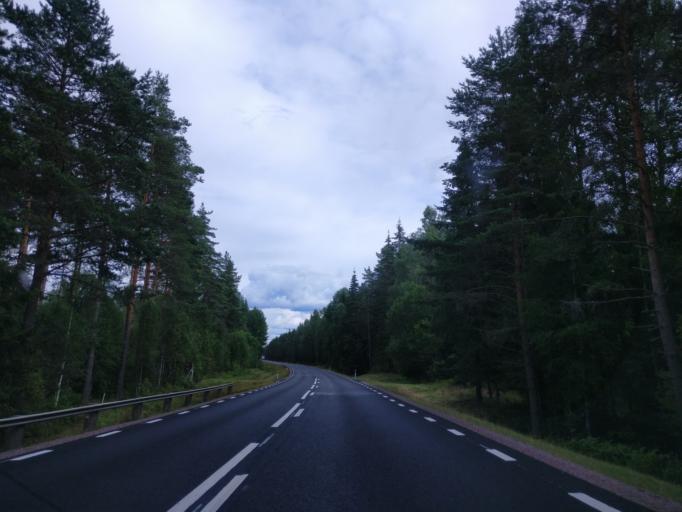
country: SE
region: Vaermland
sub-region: Hagfors Kommun
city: Hagfors
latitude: 60.0536
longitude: 13.5586
